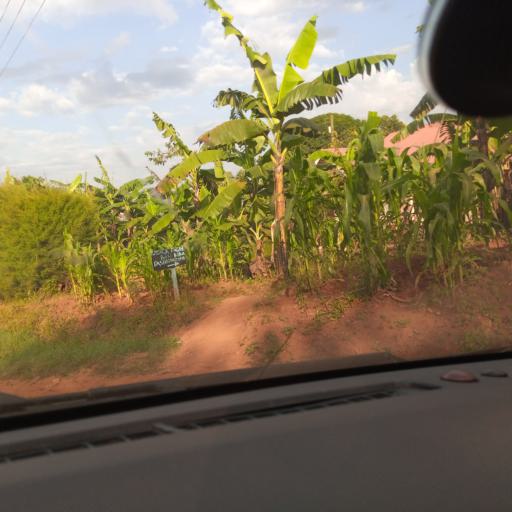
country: UG
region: Central Region
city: Masaka
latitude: -0.3460
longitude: 31.7251
